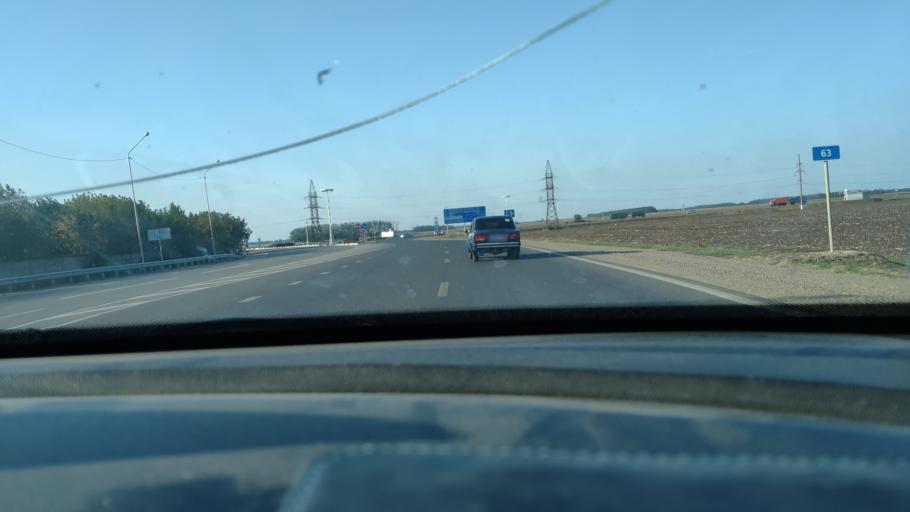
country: RU
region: Krasnodarskiy
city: Timashevsk
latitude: 45.6234
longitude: 38.9860
